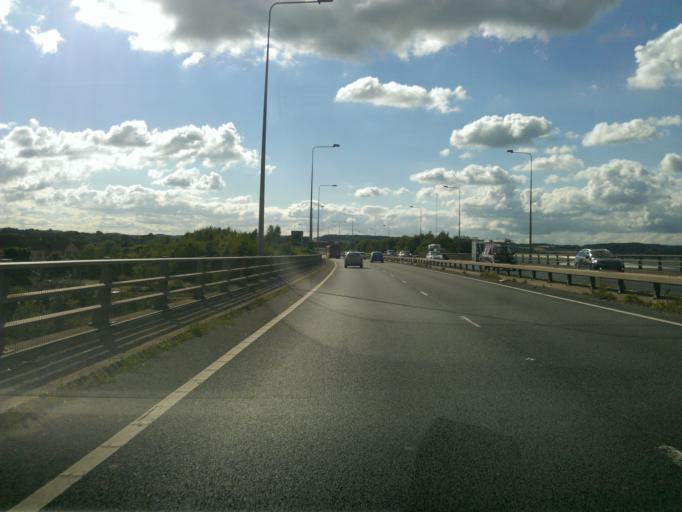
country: GB
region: England
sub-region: Staffordshire
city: Tamworth
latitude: 52.6242
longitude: -1.6958
